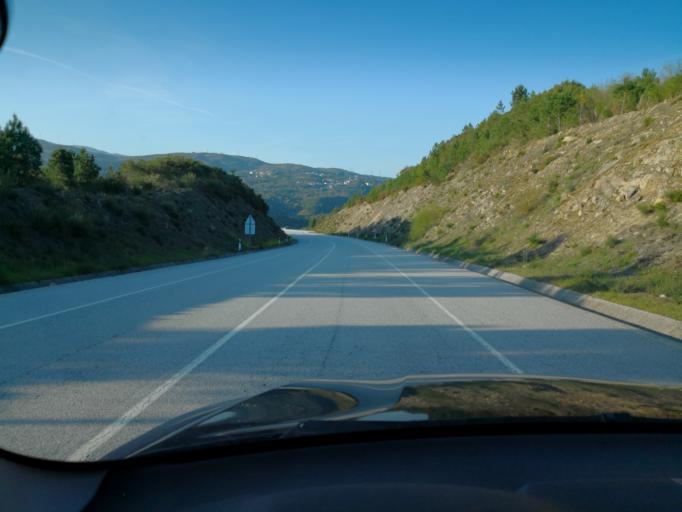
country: PT
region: Vila Real
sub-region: Vila Real
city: Vila Real
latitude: 41.3621
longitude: -7.7082
